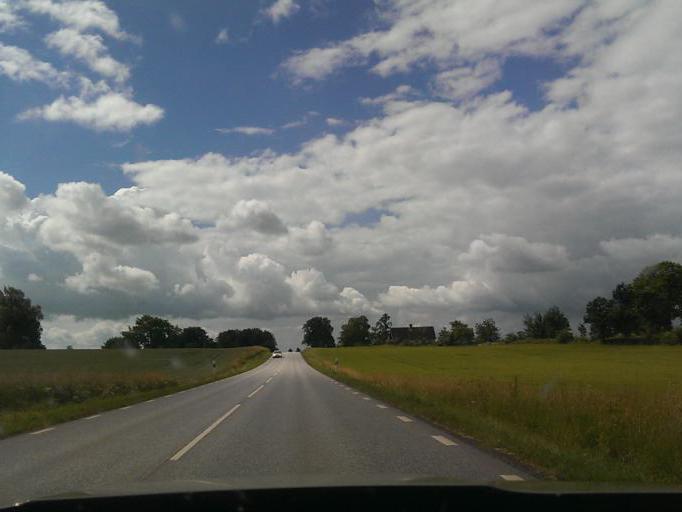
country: SE
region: Skane
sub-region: Eslovs Kommun
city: Eslov
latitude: 55.8740
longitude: 13.3132
